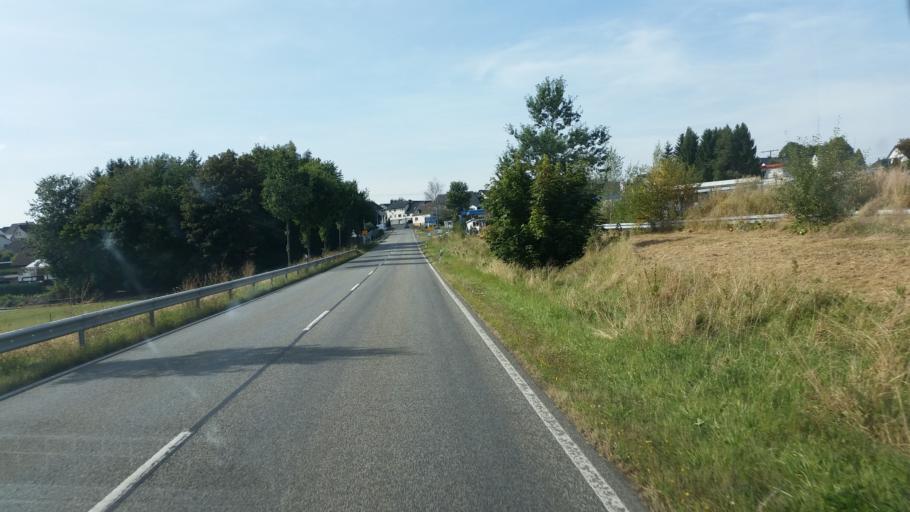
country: DE
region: Rheinland-Pfalz
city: Hohn
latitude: 50.6182
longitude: 7.9927
